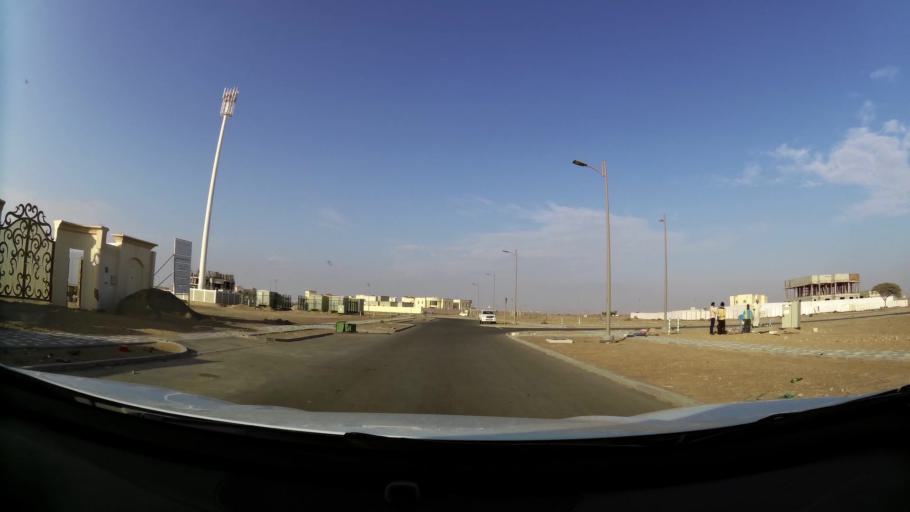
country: AE
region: Abu Dhabi
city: Al Ain
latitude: 24.1094
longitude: 55.8552
